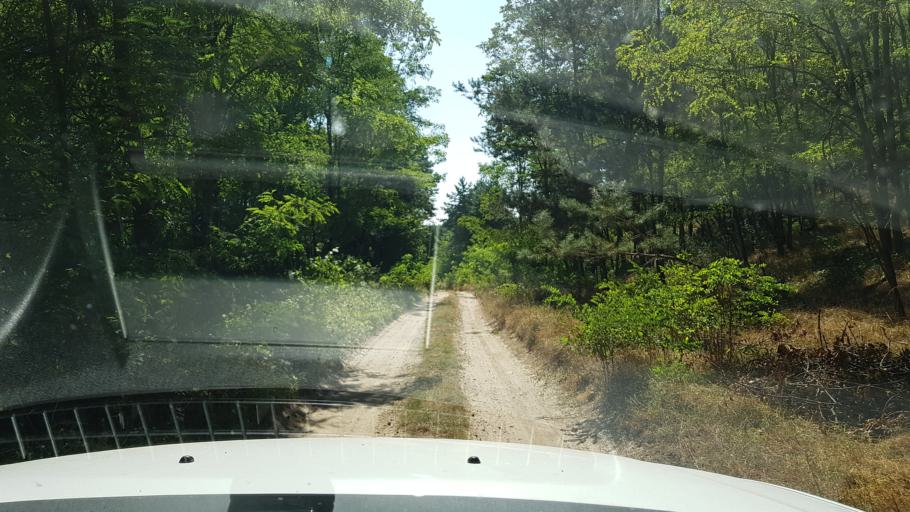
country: PL
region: West Pomeranian Voivodeship
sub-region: Powiat gryfinski
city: Cedynia
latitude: 52.8357
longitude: 14.2522
